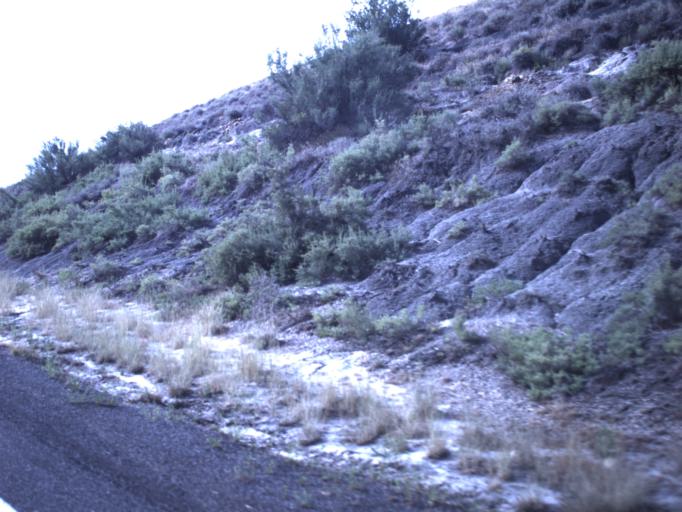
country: US
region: Utah
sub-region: Washington County
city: Hildale
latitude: 37.2618
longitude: -112.7710
